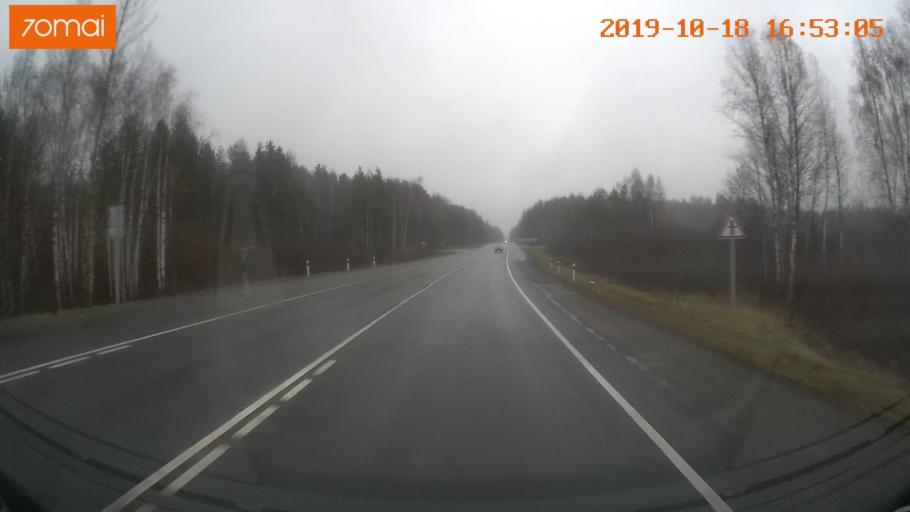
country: RU
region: Ivanovo
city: Nerl'
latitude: 56.6099
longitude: 40.5569
